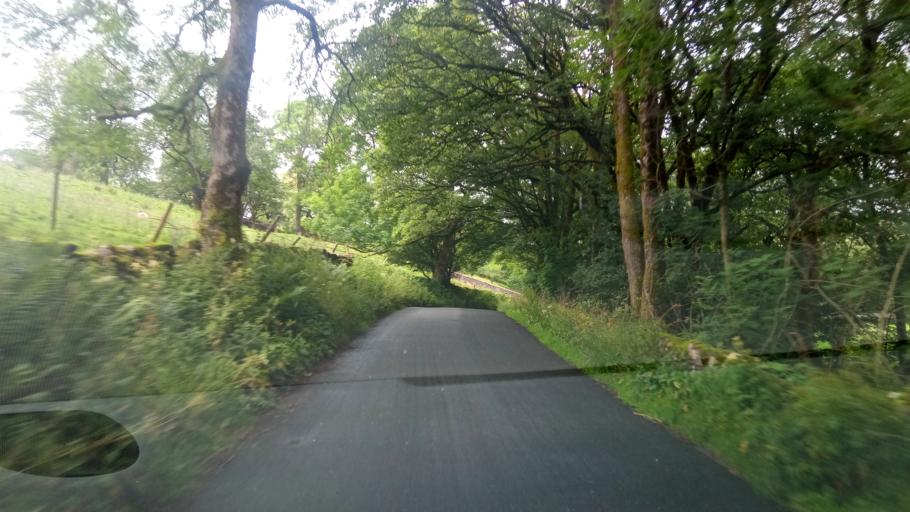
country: GB
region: England
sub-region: North Yorkshire
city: Ingleton
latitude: 54.2744
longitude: -2.3625
